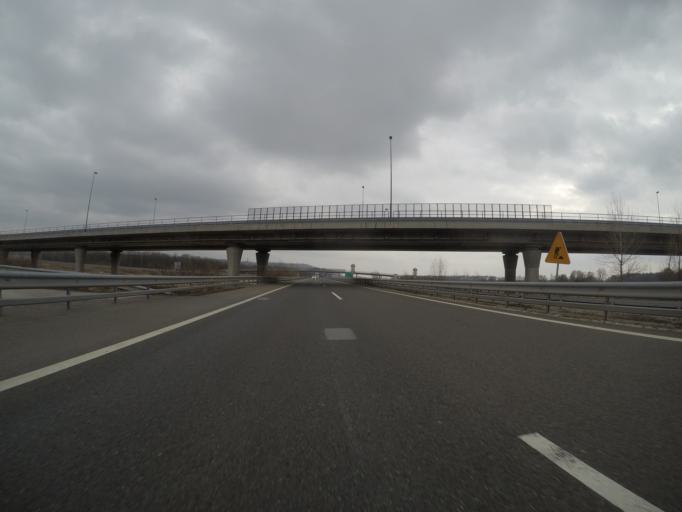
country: SI
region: Lendava-Lendva
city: Lendava
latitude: 46.5871
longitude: 16.4292
